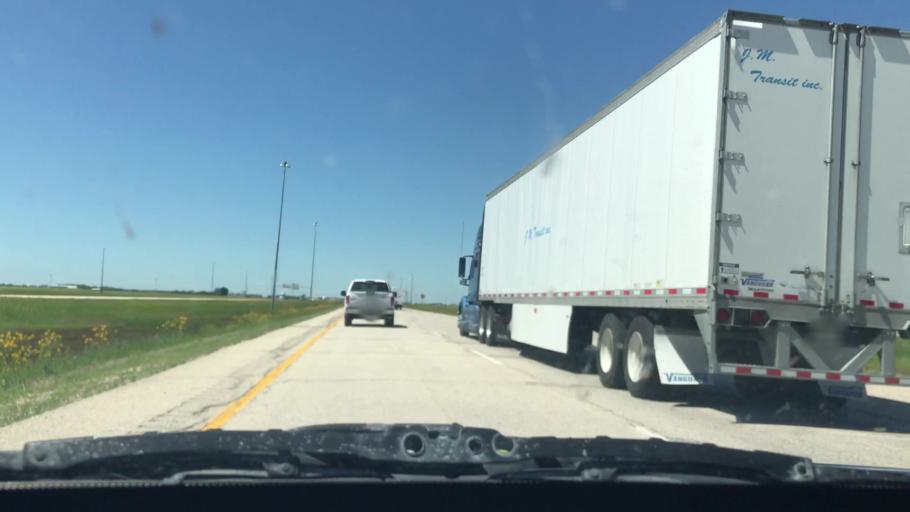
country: CA
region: Manitoba
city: Steinbach
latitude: 49.7017
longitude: -96.6471
